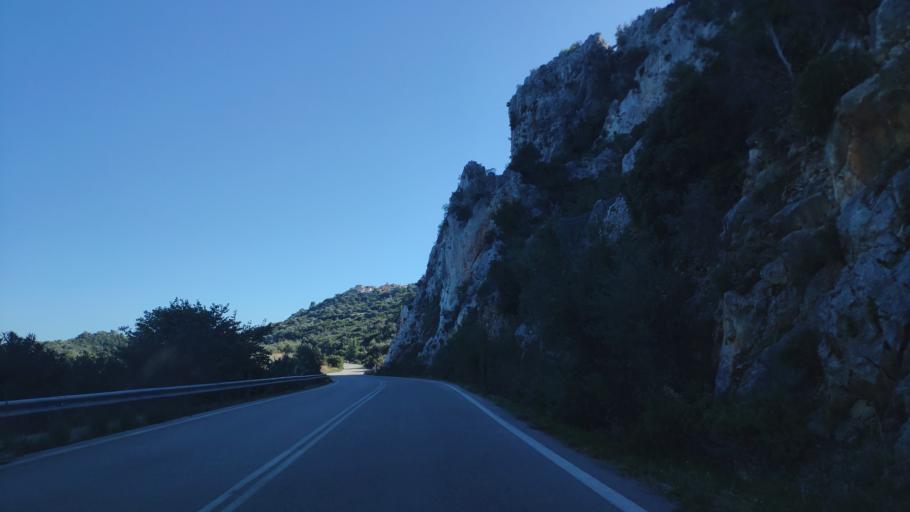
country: GR
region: Peloponnese
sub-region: Nomos Argolidos
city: Palaia Epidavros
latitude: 37.5819
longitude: 23.2333
